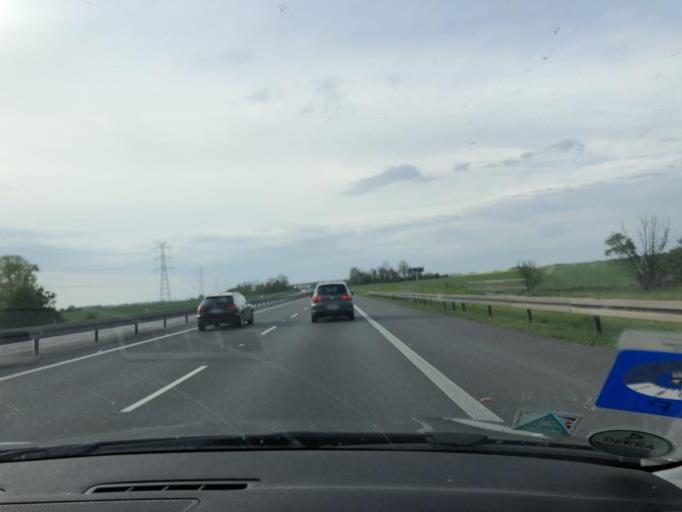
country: PL
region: Opole Voivodeship
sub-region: Powiat brzeski
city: Skarbimierz Osiedle
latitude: 50.8113
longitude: 17.3132
